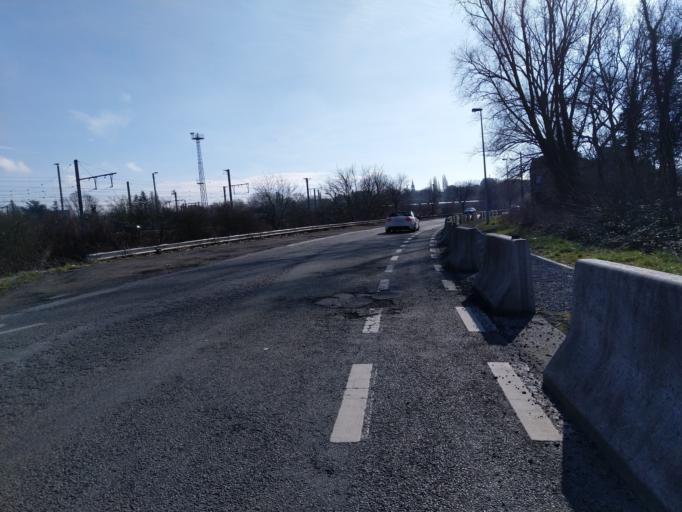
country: BE
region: Wallonia
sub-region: Province du Hainaut
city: Mons
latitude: 50.4648
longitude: 3.9472
